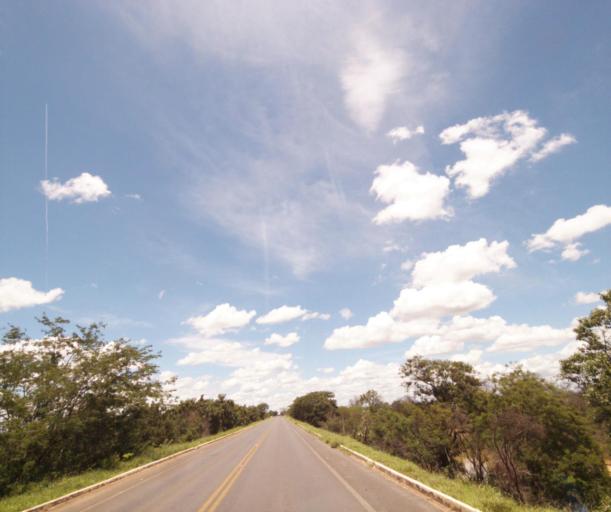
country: BR
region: Bahia
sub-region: Bom Jesus Da Lapa
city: Bom Jesus da Lapa
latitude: -13.2559
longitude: -43.4416
